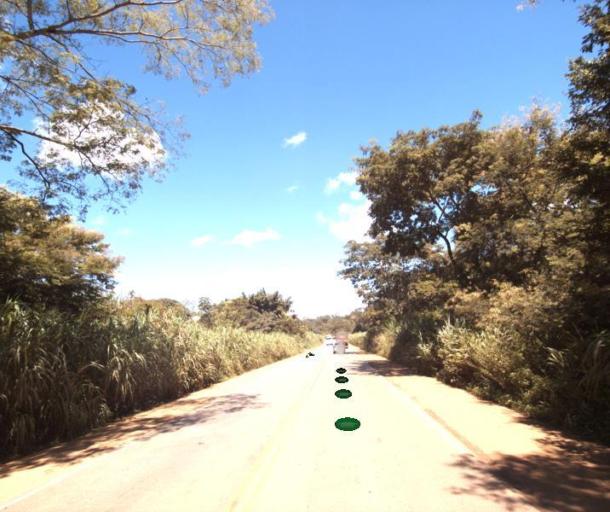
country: BR
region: Goias
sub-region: Anapolis
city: Anapolis
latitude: -16.1260
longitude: -49.0439
